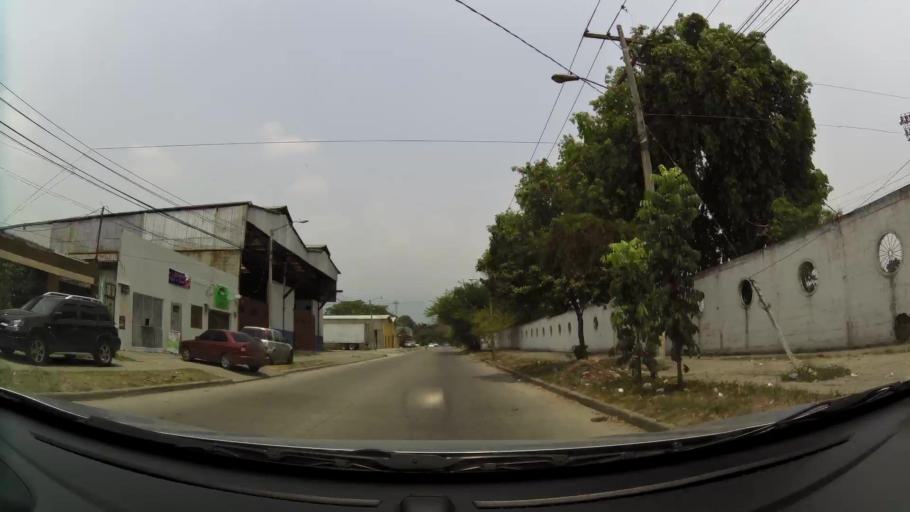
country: HN
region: Cortes
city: San Pedro Sula
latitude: 15.4856
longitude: -88.0126
